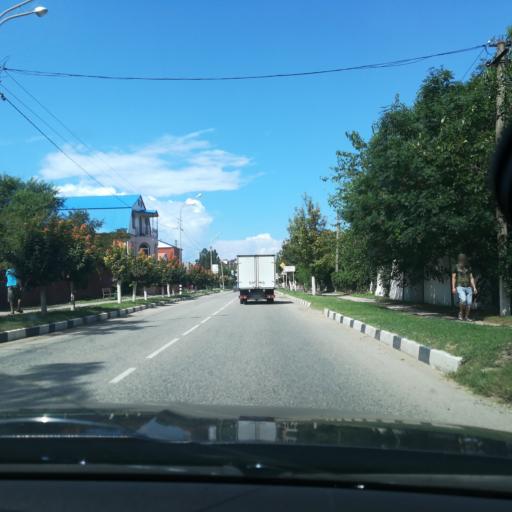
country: RU
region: Krasnodarskiy
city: Taman'
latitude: 45.2173
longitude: 36.7264
